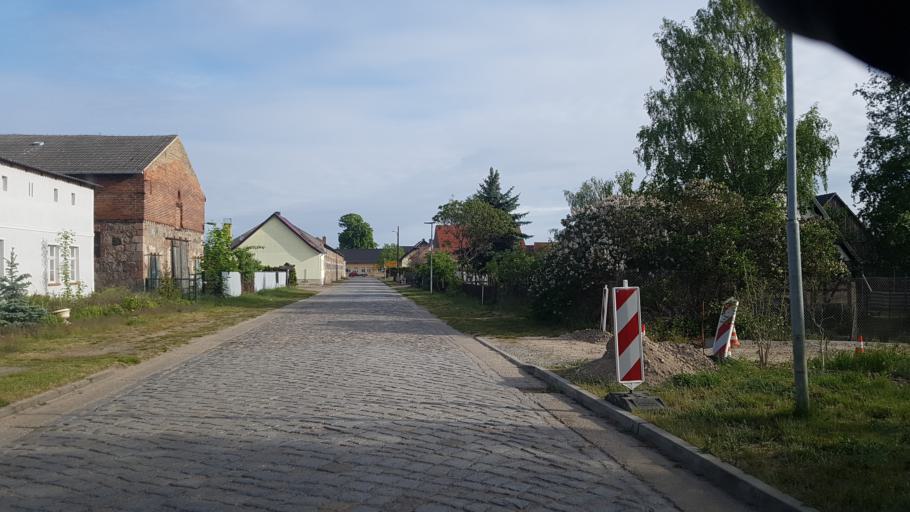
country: DE
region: Brandenburg
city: Baruth
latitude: 52.0489
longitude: 13.4708
